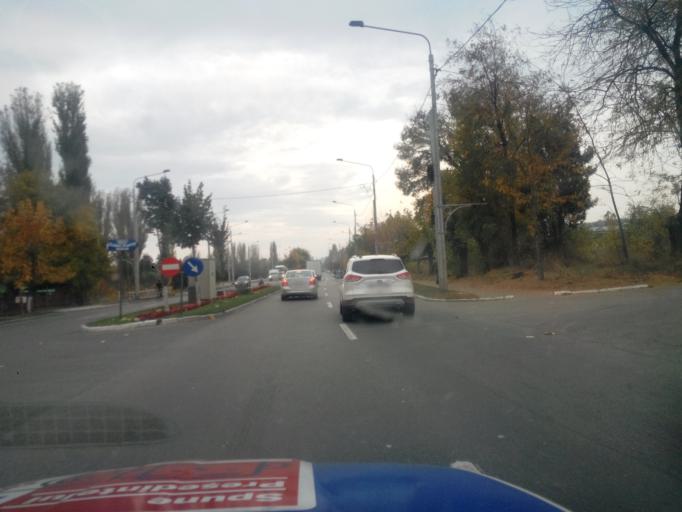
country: RO
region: Vaslui
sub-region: Municipiul Barlad
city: Barlad
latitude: 46.2470
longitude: 27.6809
